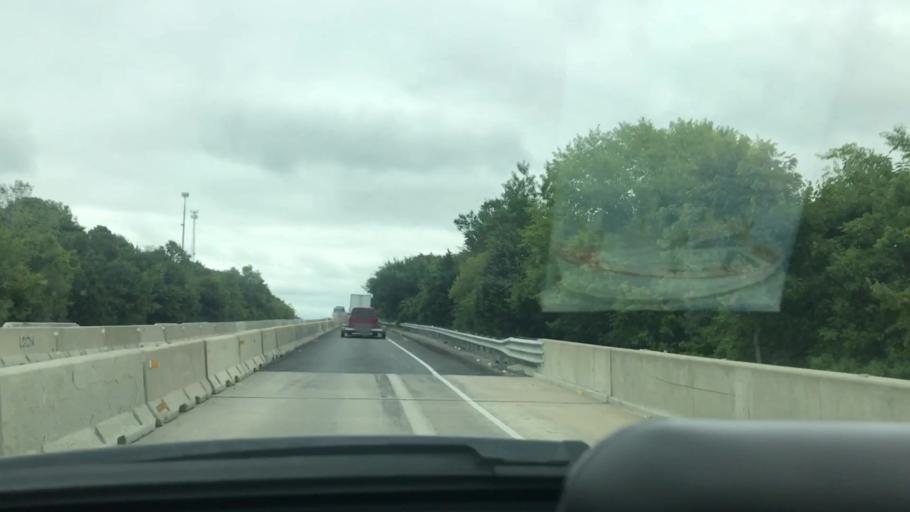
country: US
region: Oklahoma
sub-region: McIntosh County
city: Eufaula
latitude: 35.2848
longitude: -95.5931
